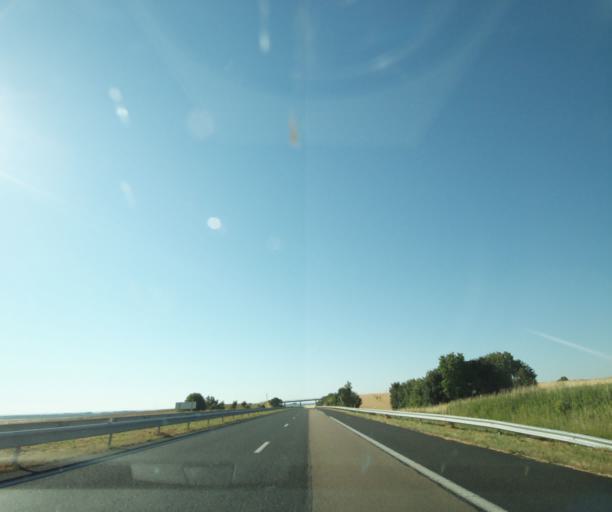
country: FR
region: Champagne-Ardenne
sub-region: Departement de l'Aube
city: La Riviere-de-Corps
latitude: 48.2579
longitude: 3.9758
